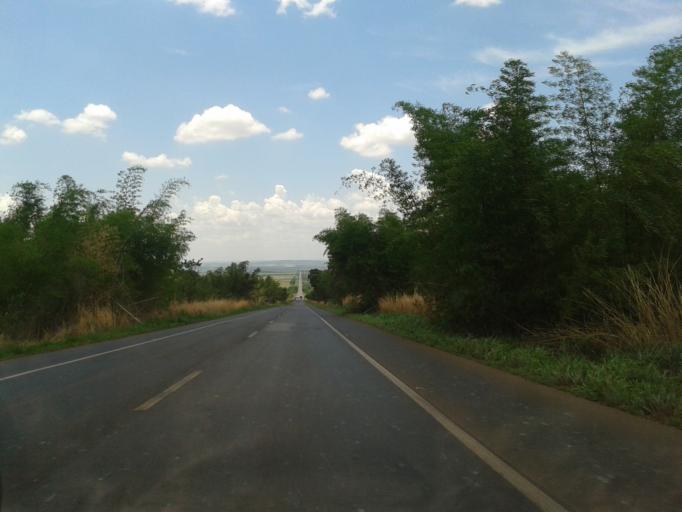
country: BR
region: Goias
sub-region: Goiatuba
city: Goiatuba
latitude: -18.2578
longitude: -49.6723
